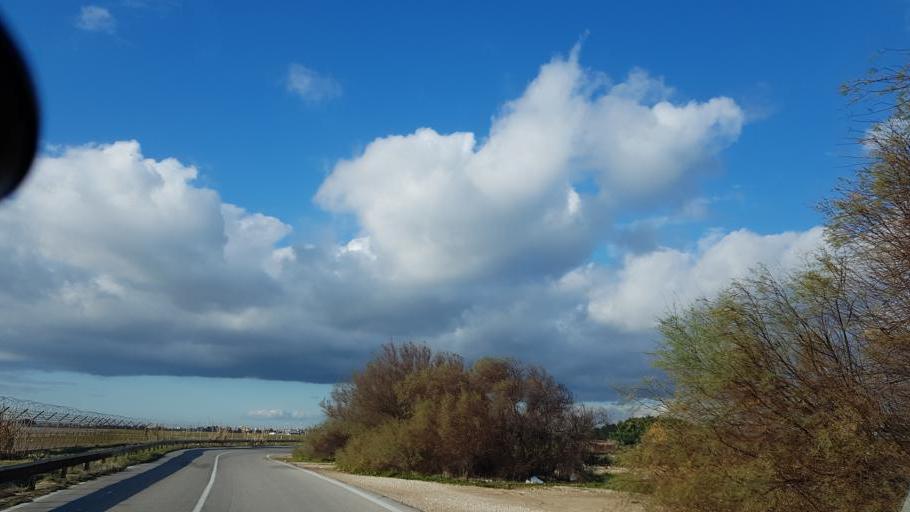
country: IT
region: Apulia
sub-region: Provincia di Brindisi
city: Materdomini
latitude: 40.6638
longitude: 17.9558
